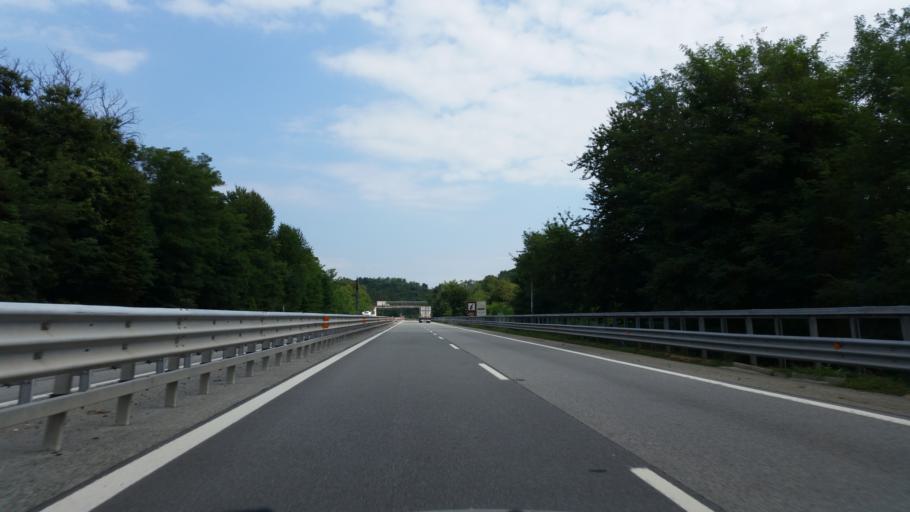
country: IT
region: Piedmont
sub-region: Provincia di Torino
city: Montalenghe
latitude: 45.3498
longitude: 7.8313
